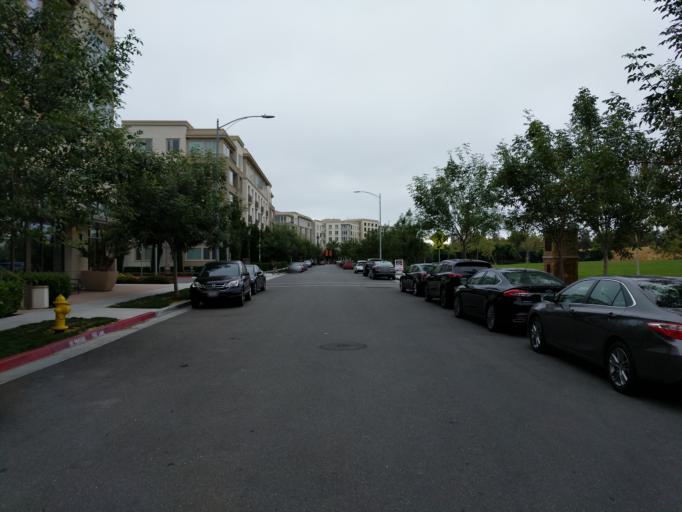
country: US
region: California
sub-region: Santa Clara County
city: Milpitas
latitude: 37.4021
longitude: -121.9448
